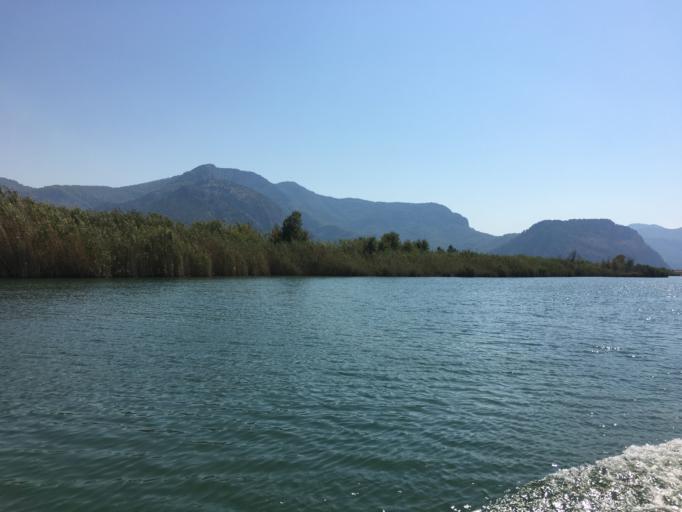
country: TR
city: Dalyan
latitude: 36.8229
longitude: 28.6345
